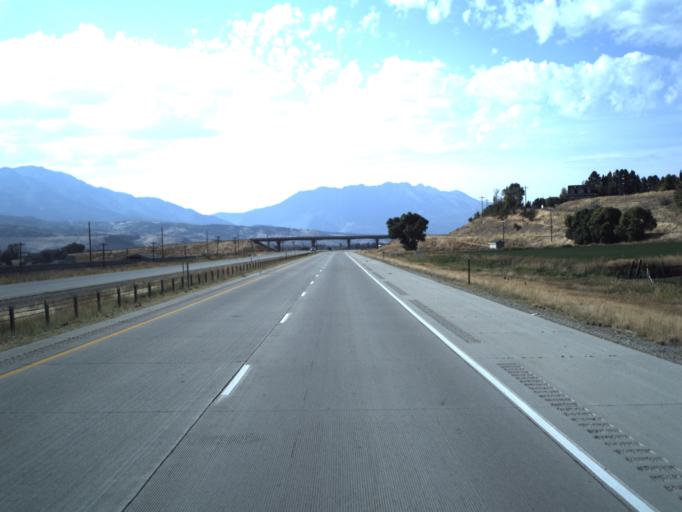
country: US
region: Utah
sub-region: Morgan County
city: Morgan
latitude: 41.0631
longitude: -111.7064
